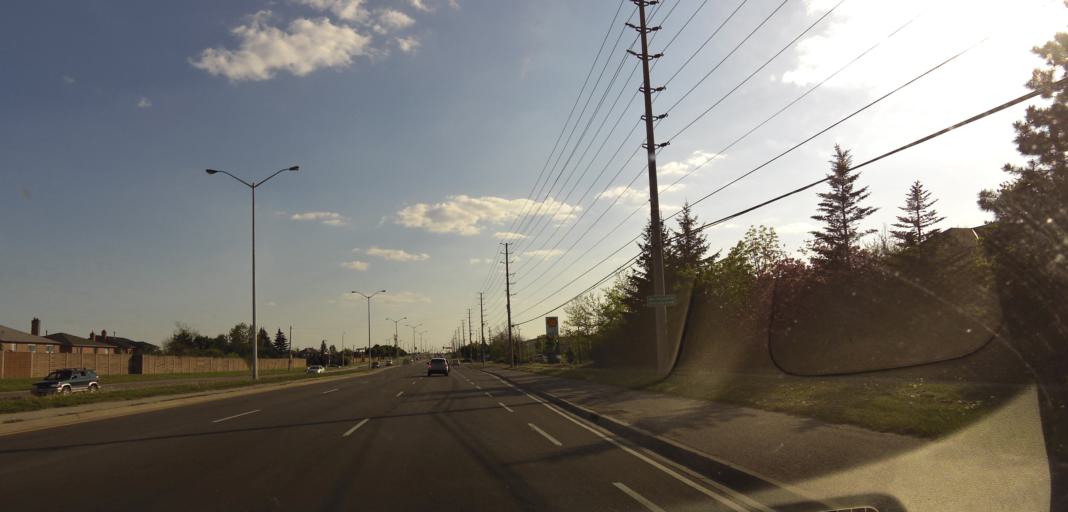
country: CA
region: Ontario
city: Brampton
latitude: 43.7316
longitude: -79.7584
